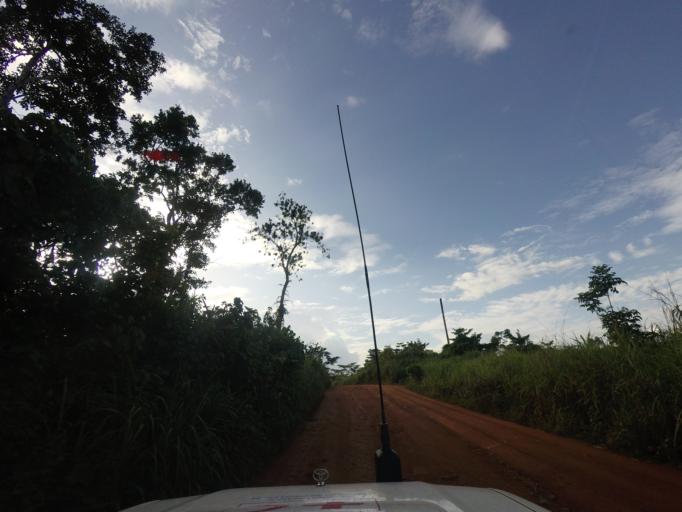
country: GN
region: Nzerekore
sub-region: Nzerekore Prefecture
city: Nzerekore
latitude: 7.6702
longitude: -8.8069
